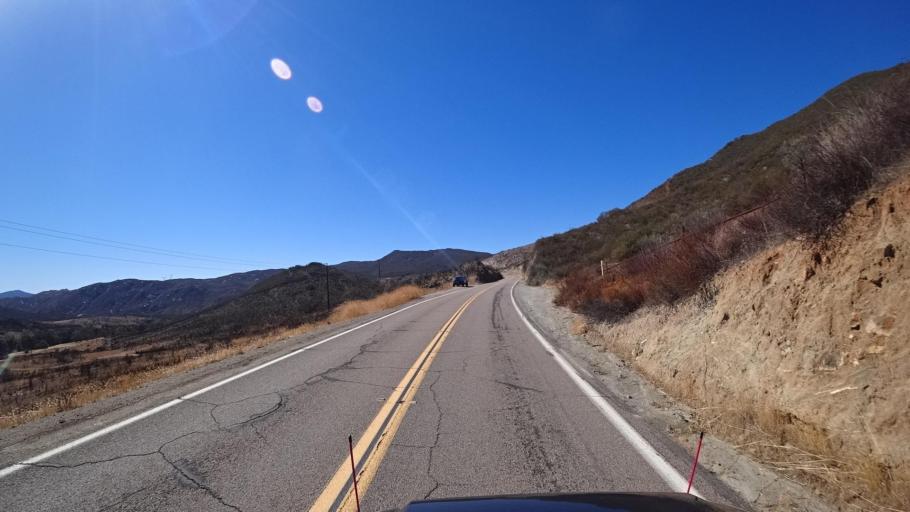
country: US
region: California
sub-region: San Diego County
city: Alpine
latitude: 32.7139
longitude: -116.7054
